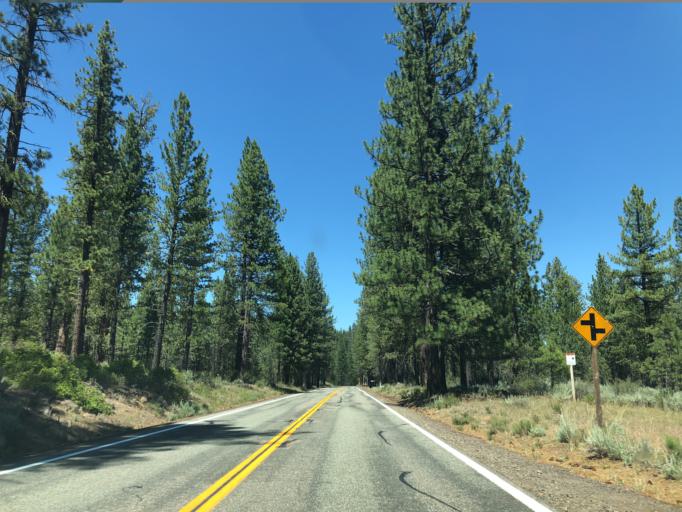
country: US
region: California
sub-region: Shasta County
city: Burney
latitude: 40.6393
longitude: -121.4730
